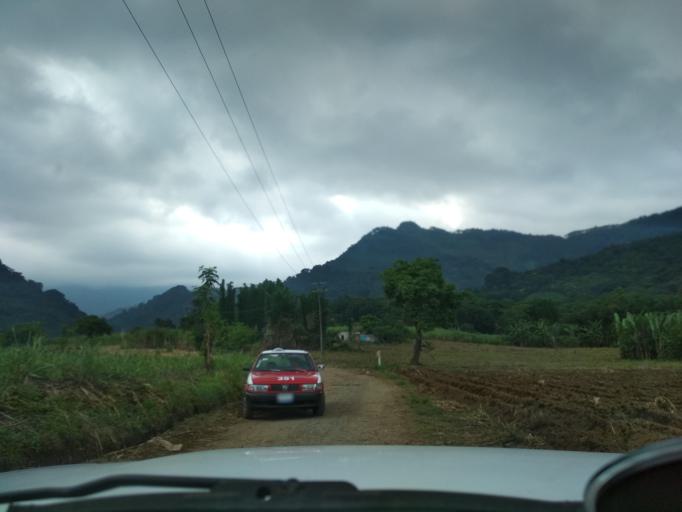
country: MX
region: Veracruz
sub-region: Fortin
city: Santa Lucia Potrerillo
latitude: 18.9501
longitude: -97.0616
